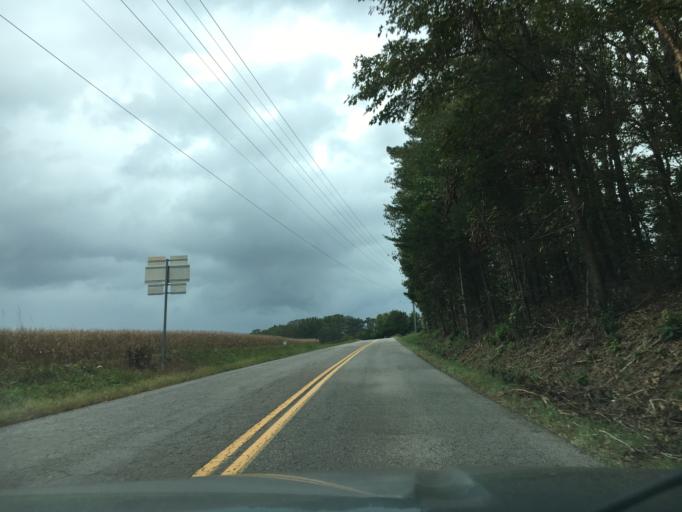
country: US
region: Virginia
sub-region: Amelia County
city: Amelia Court House
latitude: 37.3584
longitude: -77.9739
